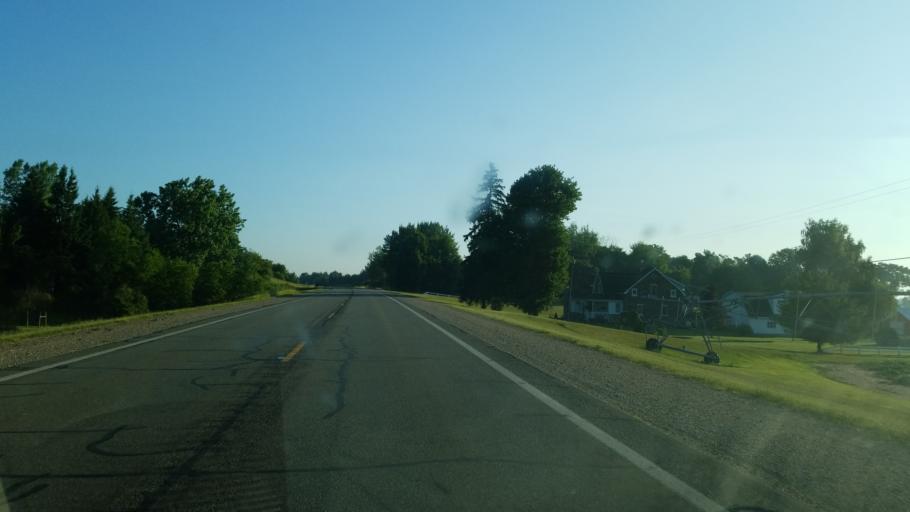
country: US
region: Michigan
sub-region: Montcalm County
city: Stanton
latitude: 43.3452
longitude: -85.0865
